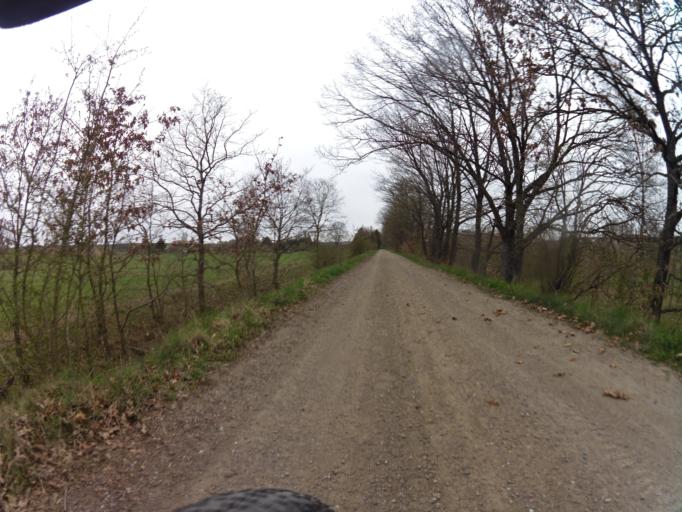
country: PL
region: West Pomeranian Voivodeship
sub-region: Powiat koszalinski
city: Bobolice
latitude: 53.9993
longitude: 16.6766
